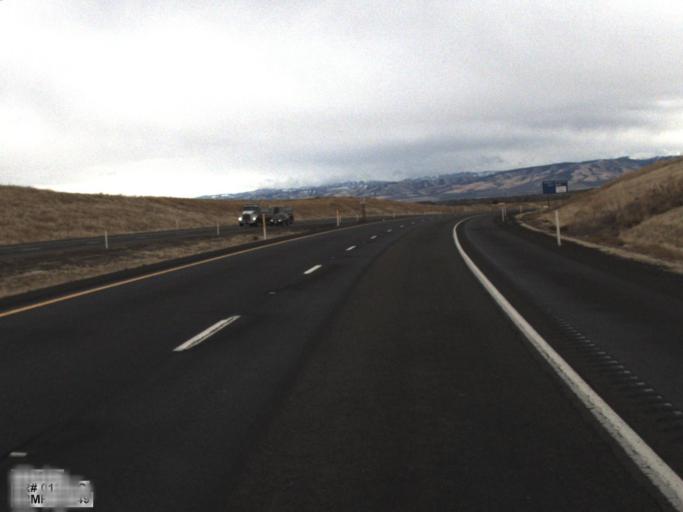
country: US
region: Washington
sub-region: Walla Walla County
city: Garrett
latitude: 46.0511
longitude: -118.5016
